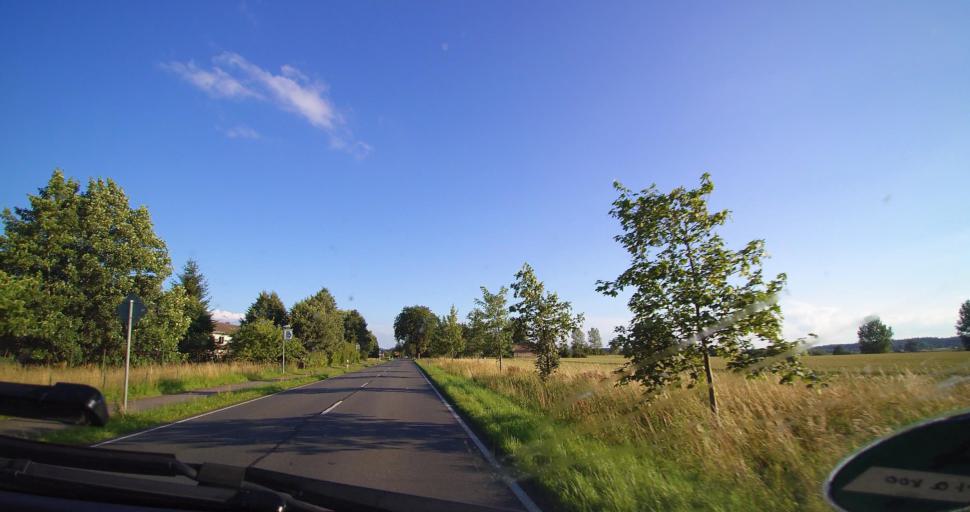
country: DE
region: Mecklenburg-Vorpommern
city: Tribsees
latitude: 54.0869
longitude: 12.7500
